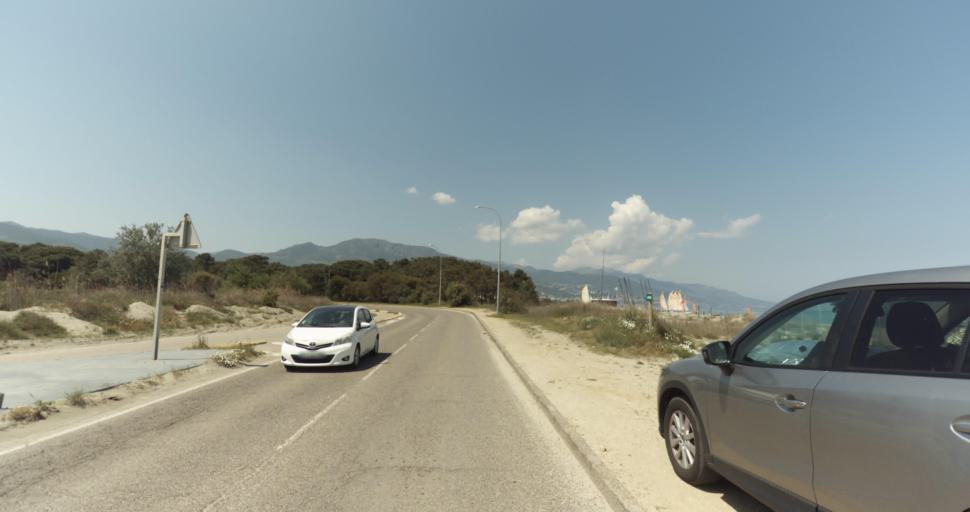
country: FR
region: Corsica
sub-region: Departement de la Haute-Corse
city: Biguglia
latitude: 42.6423
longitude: 9.4598
